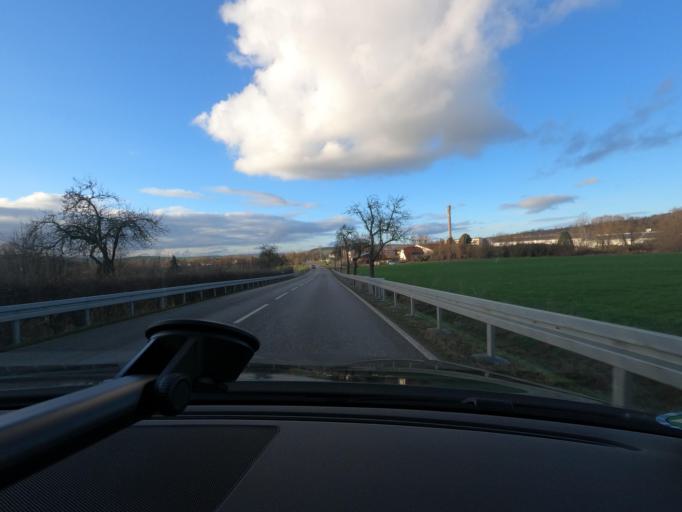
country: DE
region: Thuringia
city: Teistungen
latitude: 51.4665
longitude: 10.2782
